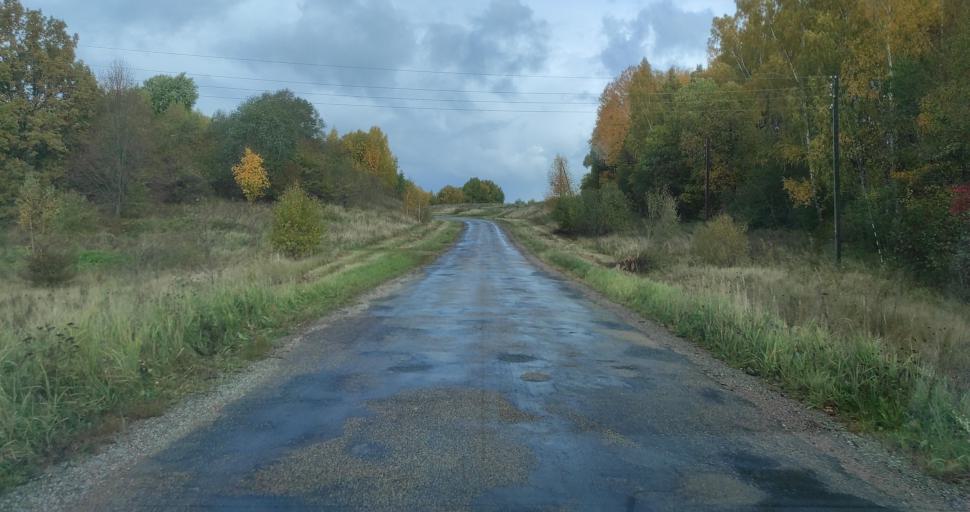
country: LV
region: Vainode
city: Vainode
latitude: 56.5641
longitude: 21.9071
